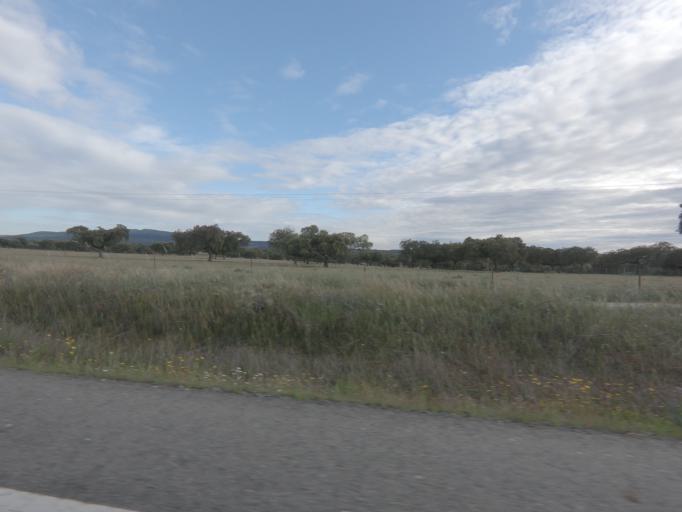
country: ES
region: Extremadura
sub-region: Provincia de Caceres
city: Torrejoncillo
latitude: 39.8833
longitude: -6.4665
